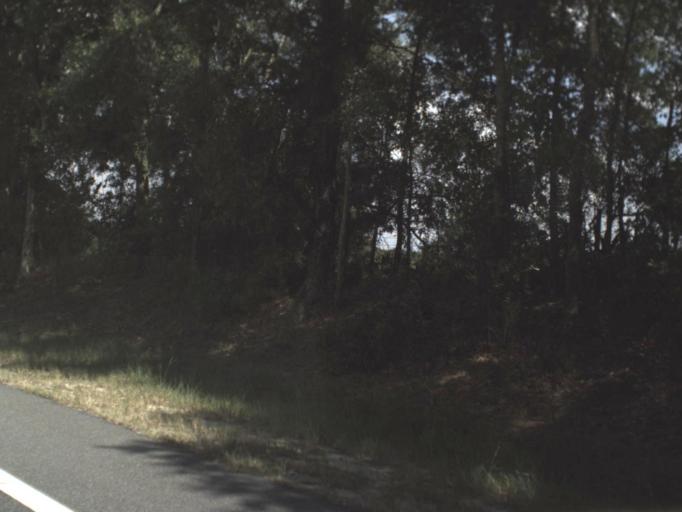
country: US
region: Florida
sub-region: Clay County
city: Keystone Heights
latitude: 29.7257
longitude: -81.9480
